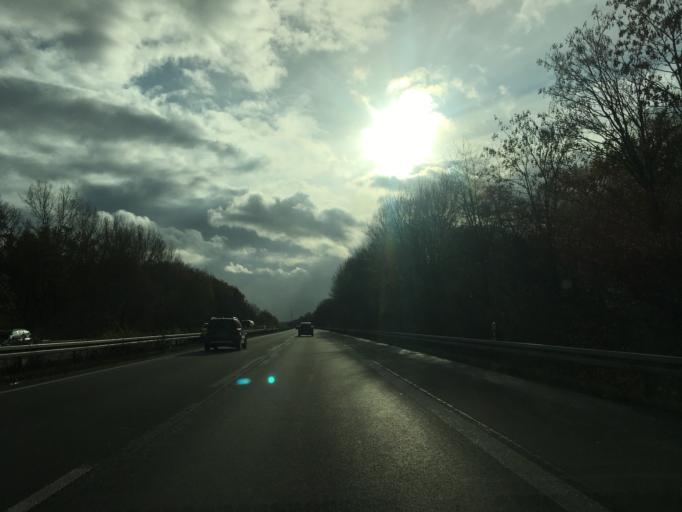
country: DE
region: North Rhine-Westphalia
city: Werne
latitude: 51.7095
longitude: 7.6593
